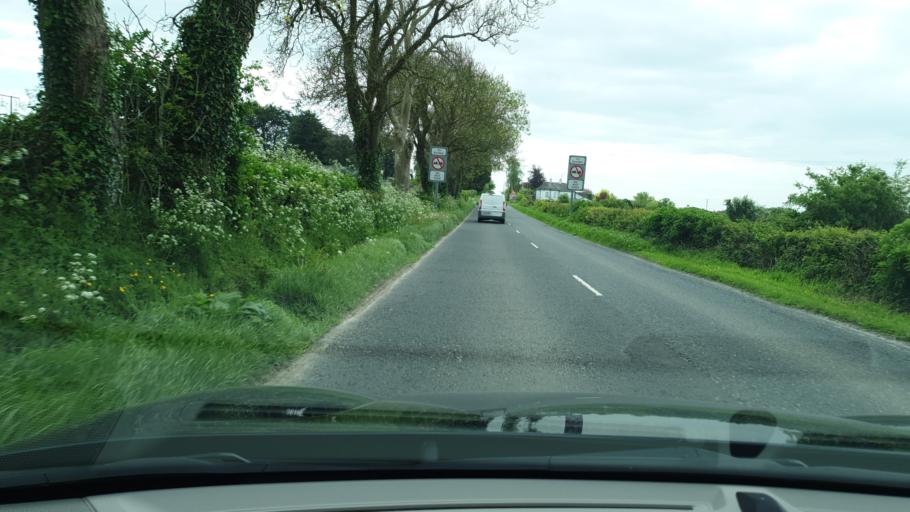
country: IE
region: Leinster
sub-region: An Mhi
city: Navan
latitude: 53.7109
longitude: -6.6901
